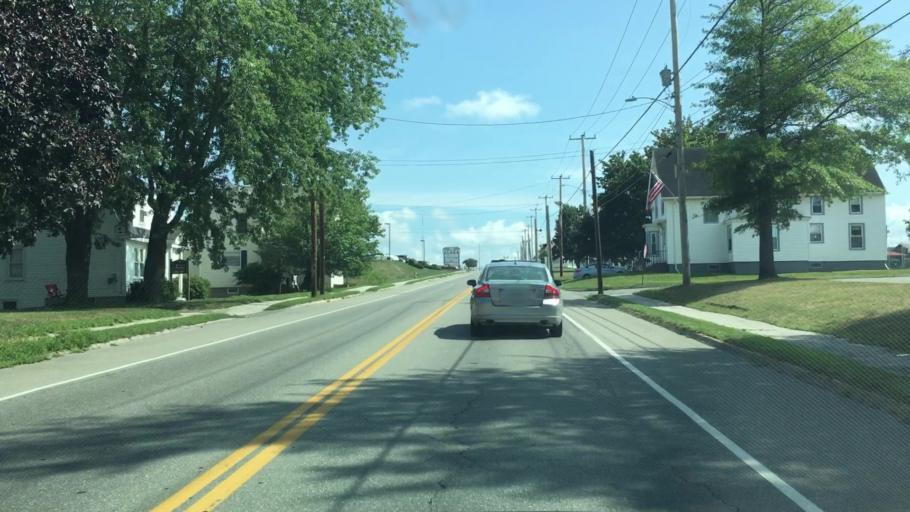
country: US
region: Maine
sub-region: Penobscot County
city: Brewer
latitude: 44.7882
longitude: -68.7549
